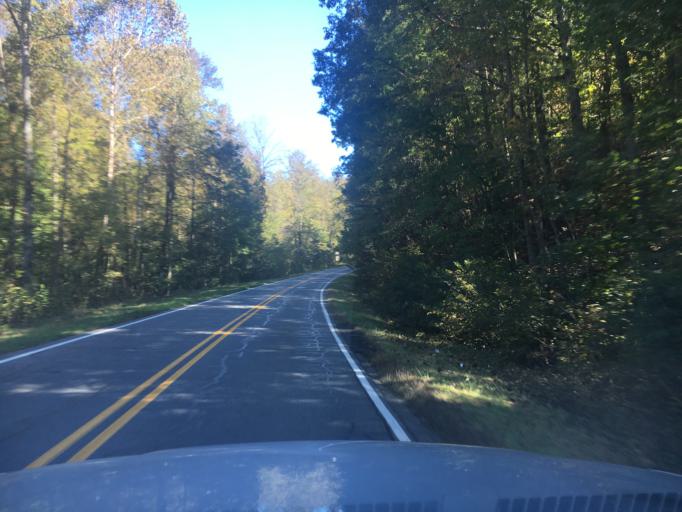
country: US
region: North Carolina
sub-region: Rutherford County
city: Spindale
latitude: 35.3453
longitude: -81.9489
